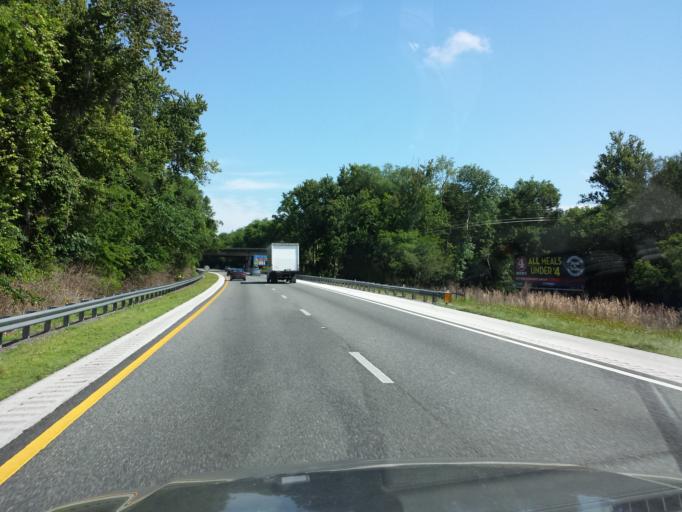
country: US
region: Florida
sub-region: Sumter County
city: Wildwood
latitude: 28.8546
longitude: -82.0902
